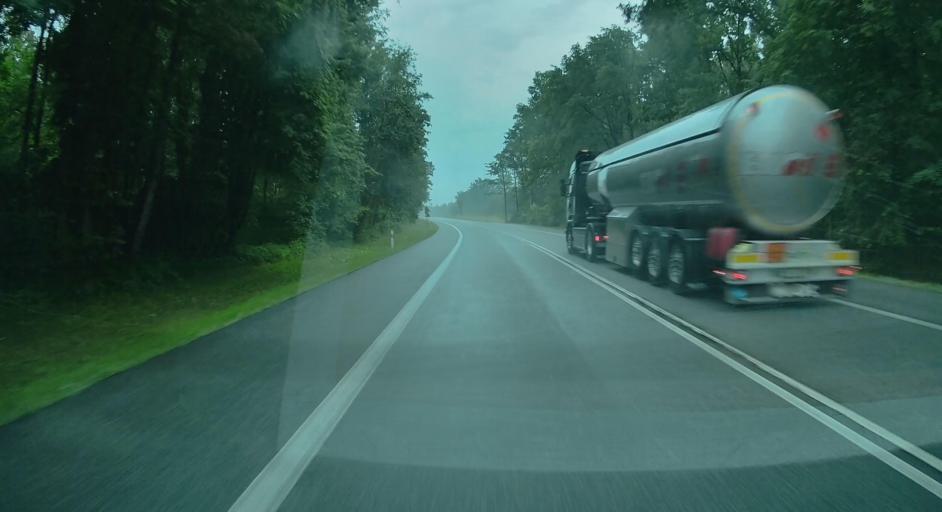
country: PL
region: Masovian Voivodeship
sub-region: Powiat siedlecki
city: Zbuczyn
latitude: 52.0835
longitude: 22.4645
